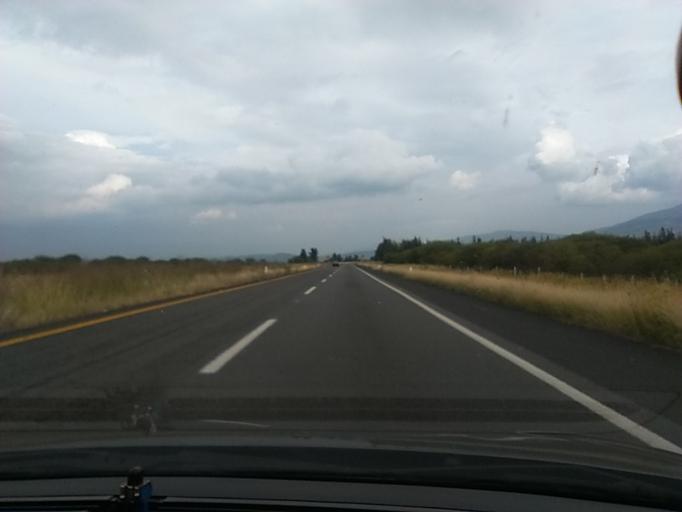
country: MX
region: Michoacan
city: Ecuandureo
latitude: 20.1834
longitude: -102.2879
